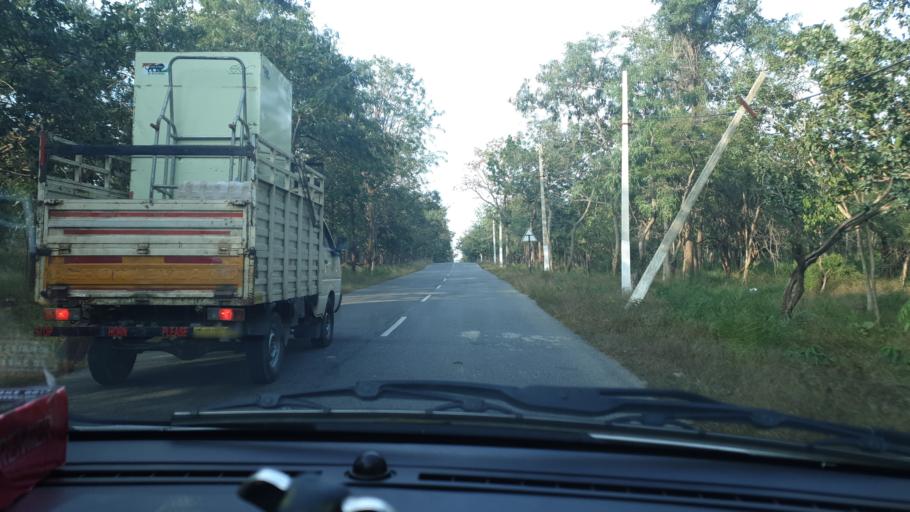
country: IN
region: Andhra Pradesh
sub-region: Kurnool
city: Srisailam
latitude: 16.2927
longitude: 78.7306
